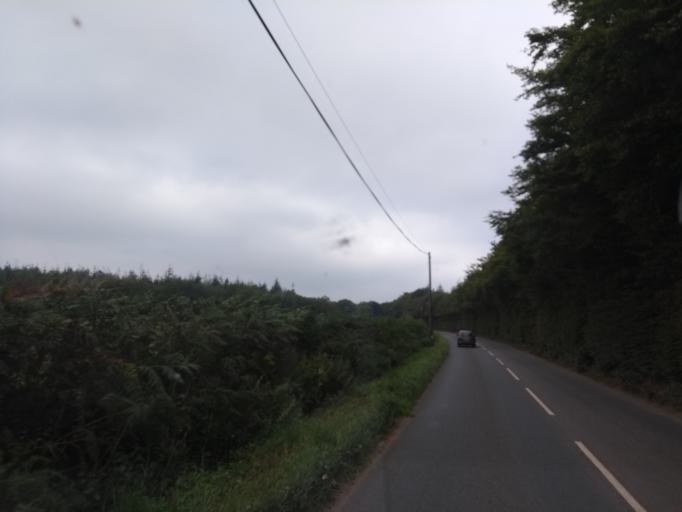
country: GB
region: England
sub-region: Somerset
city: Taunton
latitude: 50.9015
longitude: -3.0805
